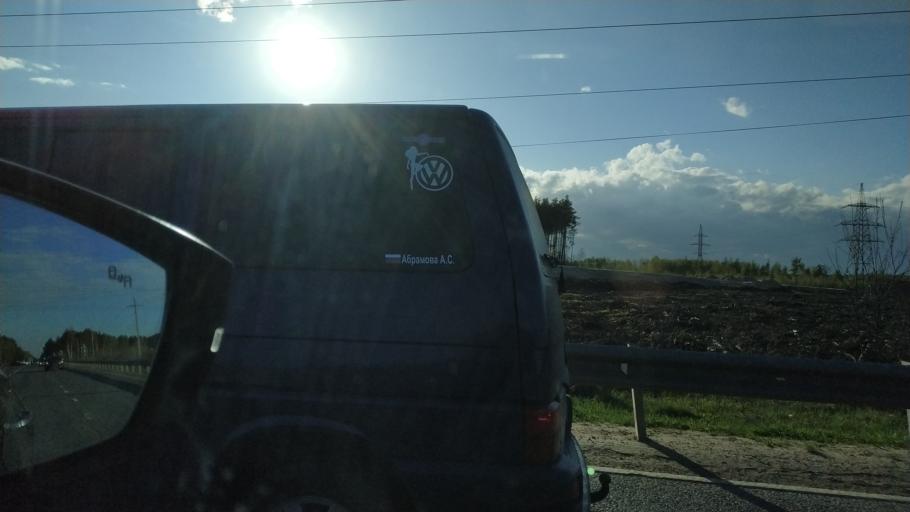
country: RU
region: Moskovskaya
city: Gzhel'
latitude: 55.6347
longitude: 38.3626
